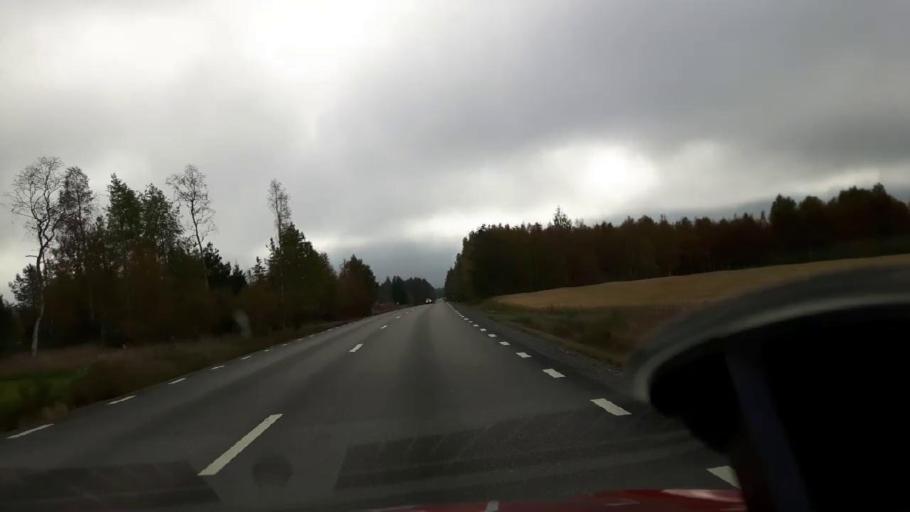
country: SE
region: Gaevleborg
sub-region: Ljusdals Kommun
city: Farila
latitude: 61.8618
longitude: 15.7407
